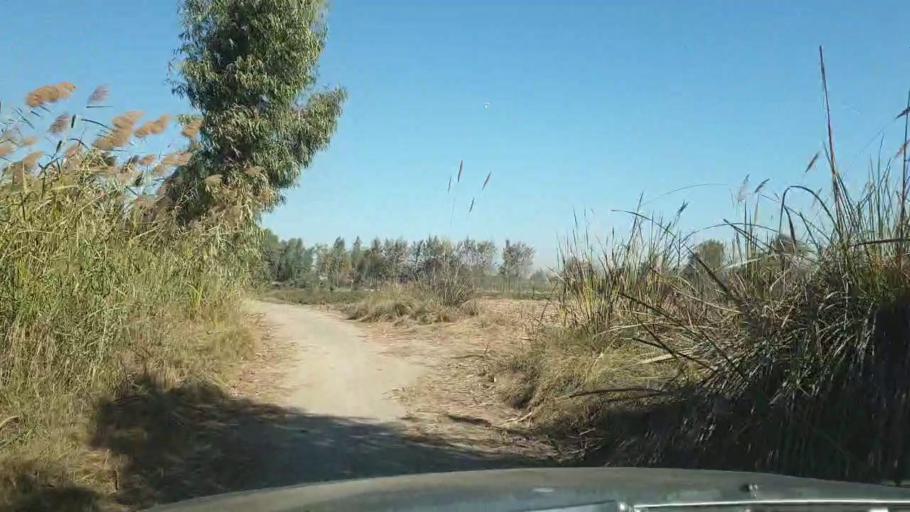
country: PK
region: Sindh
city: Ghotki
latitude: 28.0316
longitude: 69.2884
